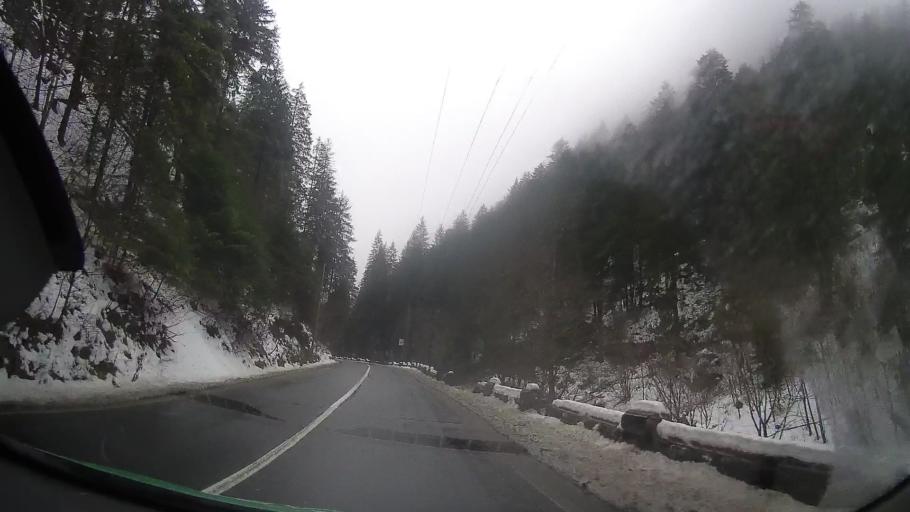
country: RO
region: Neamt
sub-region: Comuna Bicaz Chei
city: Bicaz Chei
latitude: 46.8009
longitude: 25.8009
